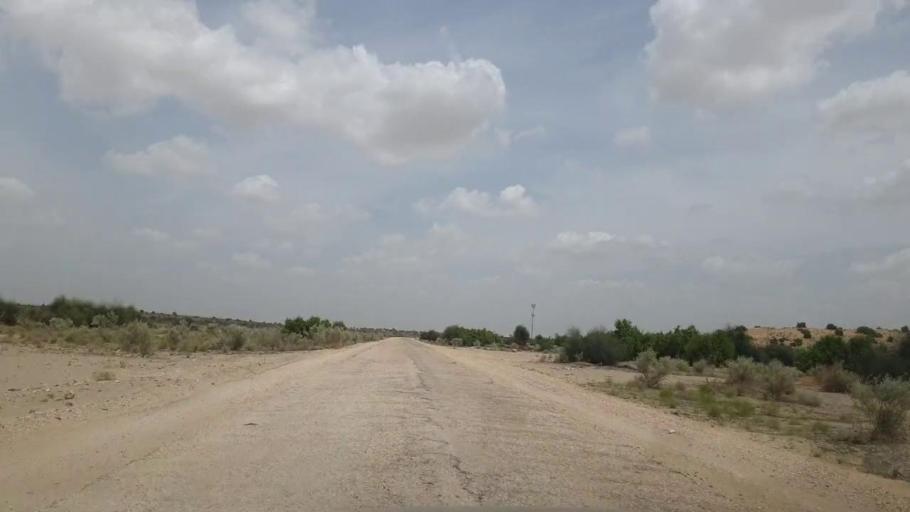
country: PK
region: Sindh
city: Kot Diji
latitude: 27.2027
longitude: 69.1466
